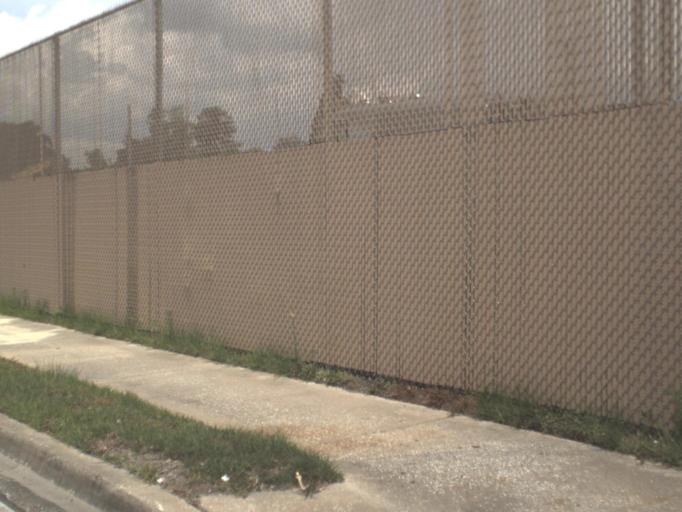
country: US
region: Florida
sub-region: Columbia County
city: Lake City
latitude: 30.1969
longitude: -82.6372
